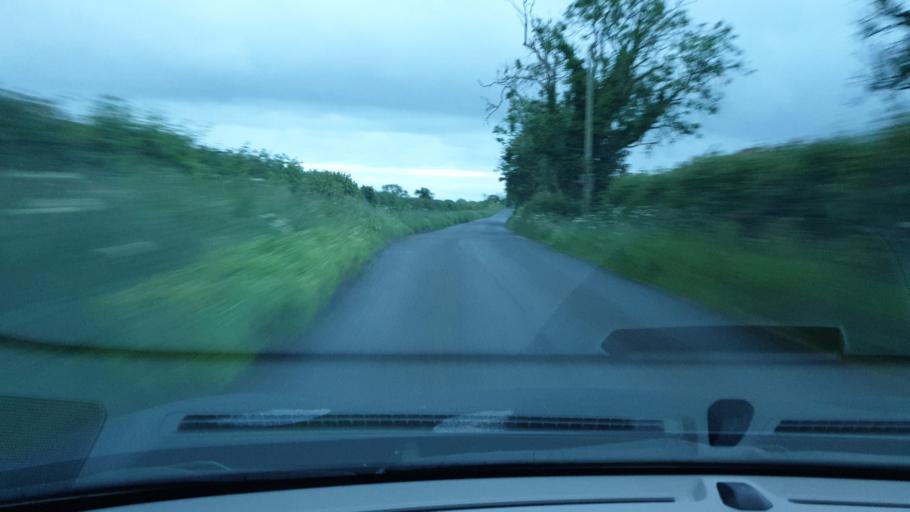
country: IE
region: Leinster
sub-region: An Mhi
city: Ashbourne
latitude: 53.5204
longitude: -6.3433
